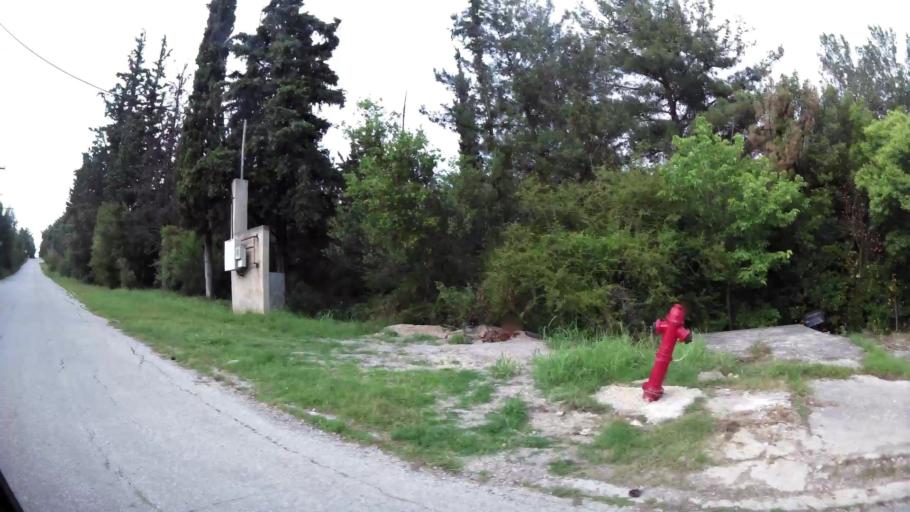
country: GR
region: Central Macedonia
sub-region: Nomos Thessalonikis
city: Oraiokastro
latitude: 40.7336
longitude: 22.9131
